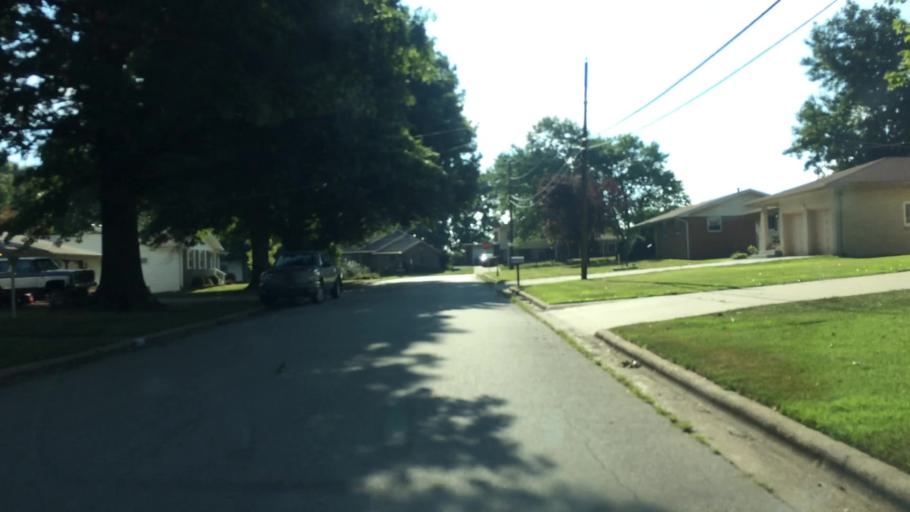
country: US
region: Missouri
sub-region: Greene County
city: Springfield
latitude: 37.2555
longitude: -93.2679
